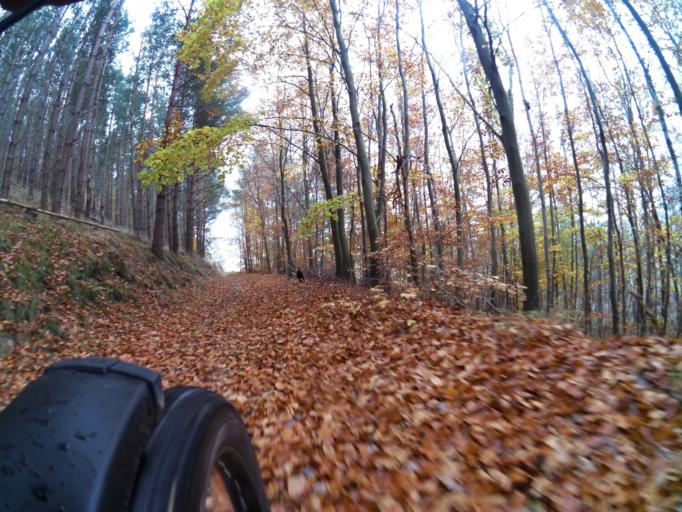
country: PL
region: Pomeranian Voivodeship
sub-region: Powiat wejherowski
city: Gniewino
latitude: 54.7514
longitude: 18.0855
